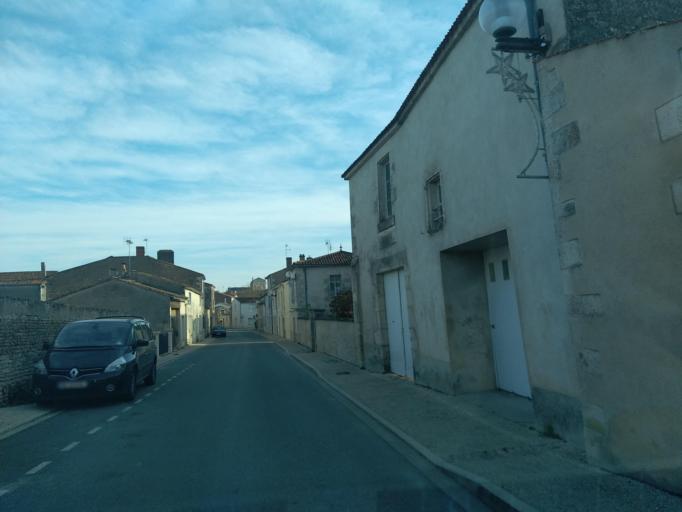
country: FR
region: Pays de la Loire
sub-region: Departement de la Vendee
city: Maillezais
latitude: 46.3725
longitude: -0.7432
